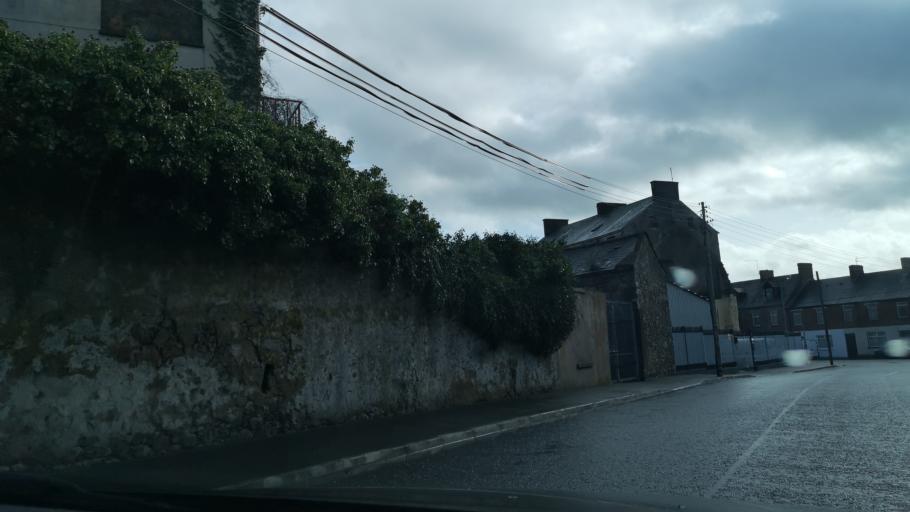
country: GB
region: Northern Ireland
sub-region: Newry and Mourne District
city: Newry
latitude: 54.1791
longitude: -6.3428
